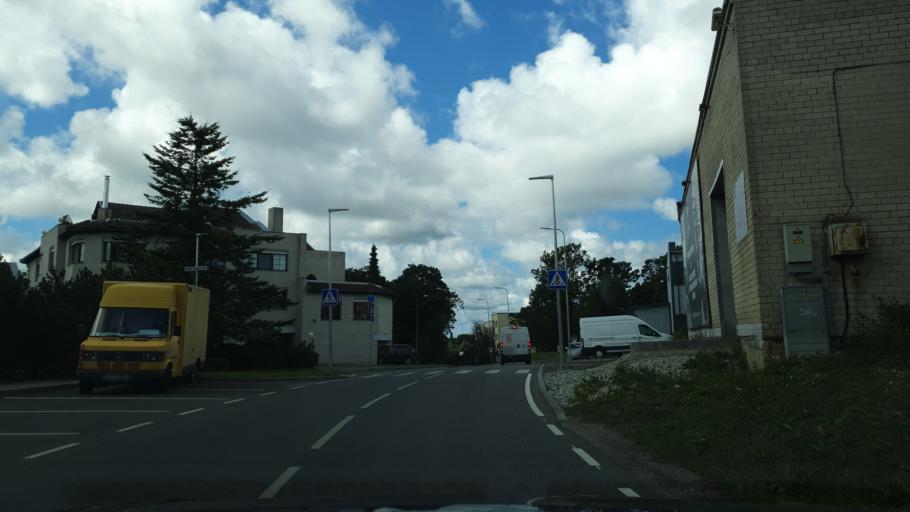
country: EE
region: Harju
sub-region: Viimsi vald
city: Viimsi
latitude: 59.5027
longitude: 24.8411
